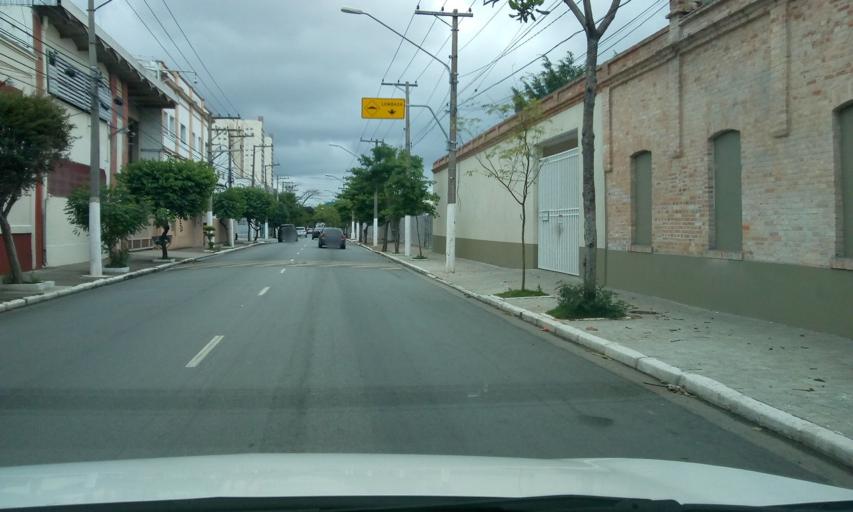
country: BR
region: Sao Paulo
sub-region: Sao Paulo
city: Sao Paulo
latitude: -23.5597
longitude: -46.6063
